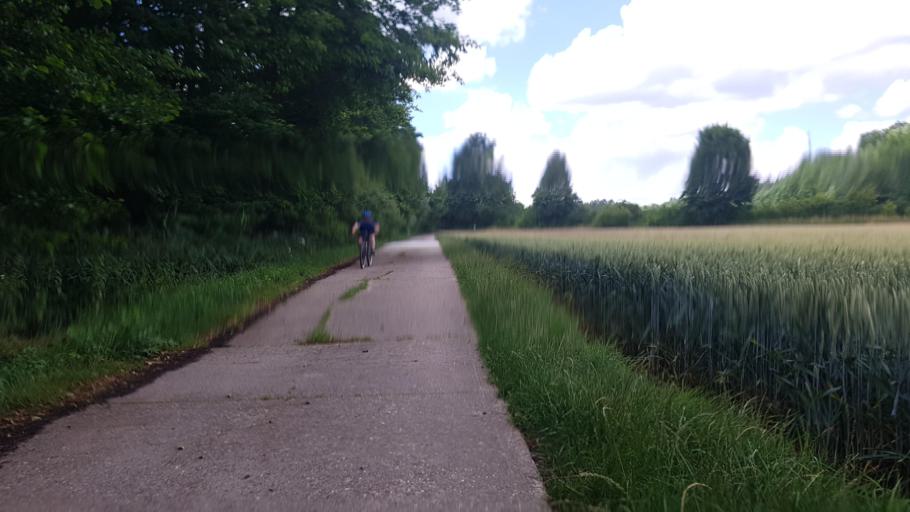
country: DE
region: Baden-Wuerttemberg
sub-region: Karlsruhe Region
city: Zaisenhausen
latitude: 49.1676
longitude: 8.7851
